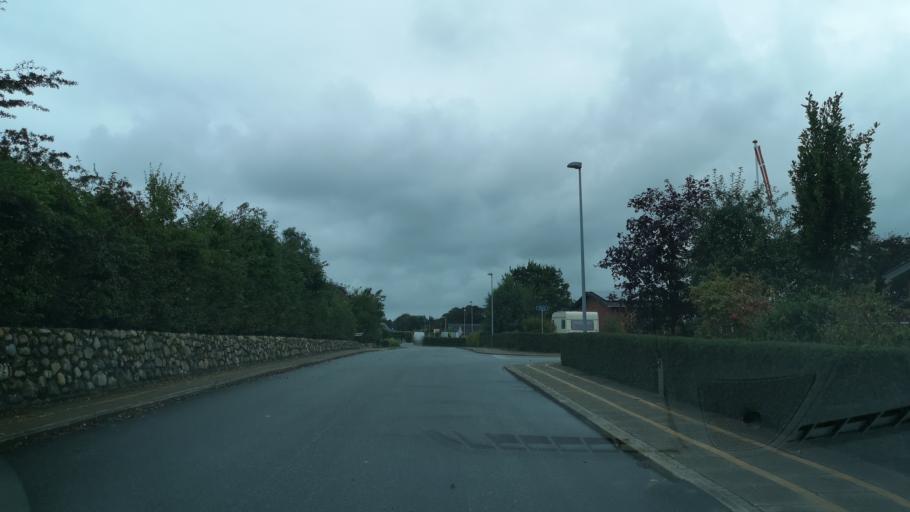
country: DK
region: Central Jutland
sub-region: Ringkobing-Skjern Kommune
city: Videbaek
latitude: 56.0869
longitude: 8.7008
